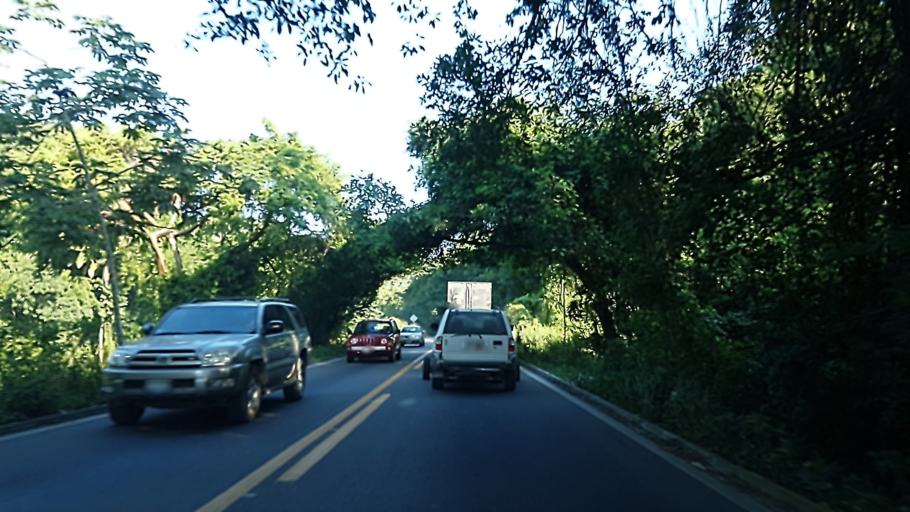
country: MX
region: Nayarit
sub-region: Bahia de Banderas
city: Lo de Marcos
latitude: 20.8869
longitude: -105.4125
